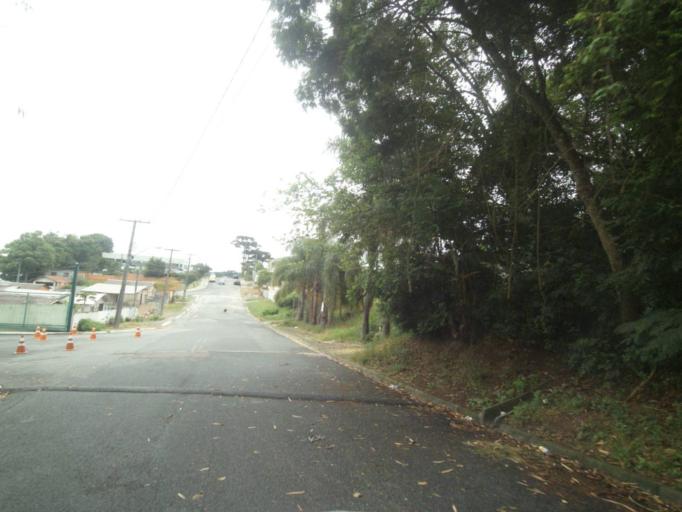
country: BR
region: Parana
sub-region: Curitiba
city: Curitiba
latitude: -25.4235
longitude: -49.3181
